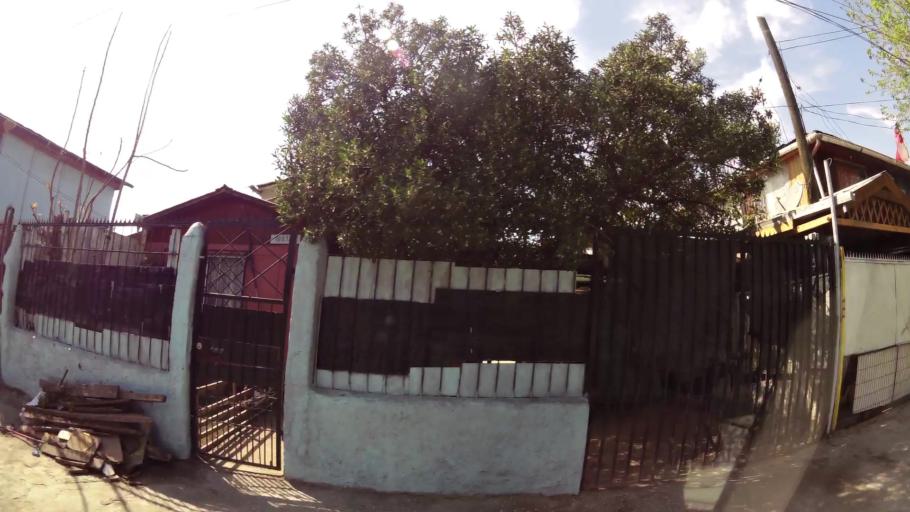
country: CL
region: Santiago Metropolitan
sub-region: Provincia de Santiago
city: La Pintana
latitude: -33.5593
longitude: -70.6486
